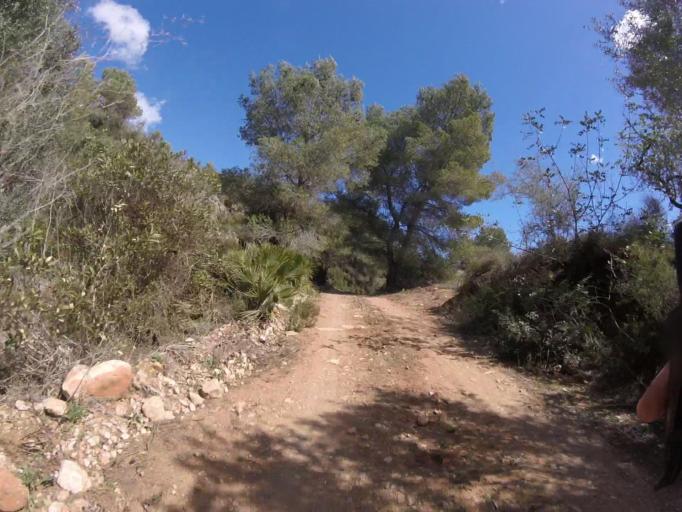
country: ES
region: Valencia
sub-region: Provincia de Castello
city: Orpesa/Oropesa del Mar
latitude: 40.1674
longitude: 0.1288
